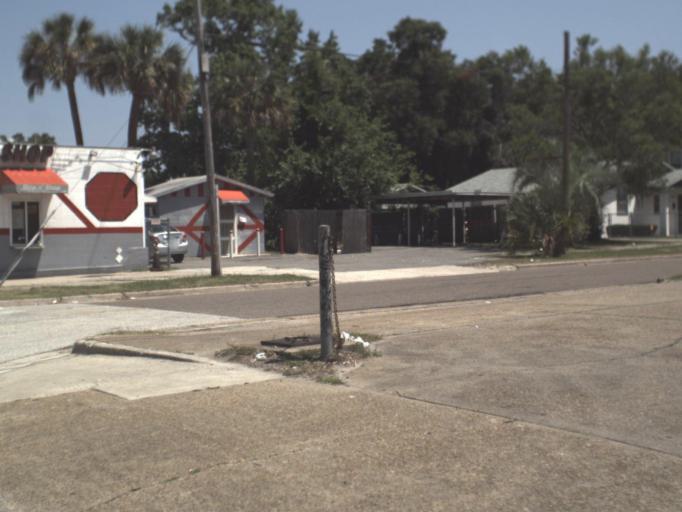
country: US
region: Florida
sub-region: Duval County
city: Jacksonville
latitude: 30.3773
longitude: -81.6682
